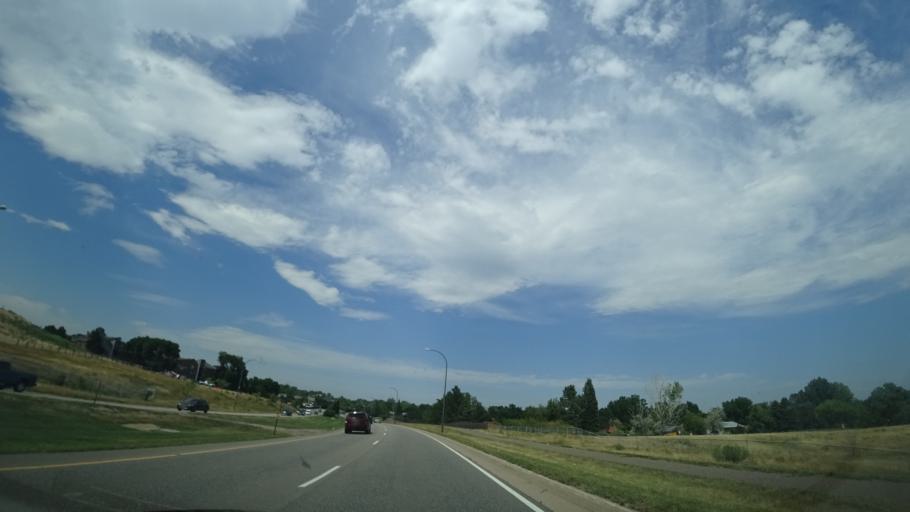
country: US
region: Colorado
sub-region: Jefferson County
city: Lakewood
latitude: 39.6934
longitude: -105.1136
